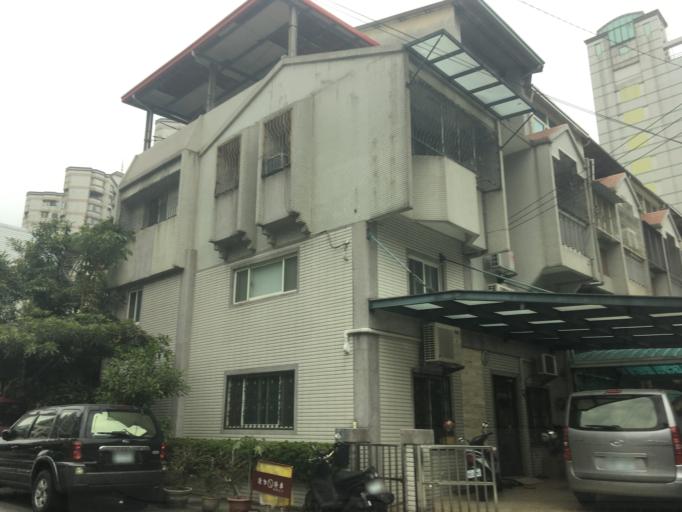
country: TW
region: Taiwan
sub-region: Taichung City
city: Taichung
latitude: 24.1766
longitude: 120.6883
